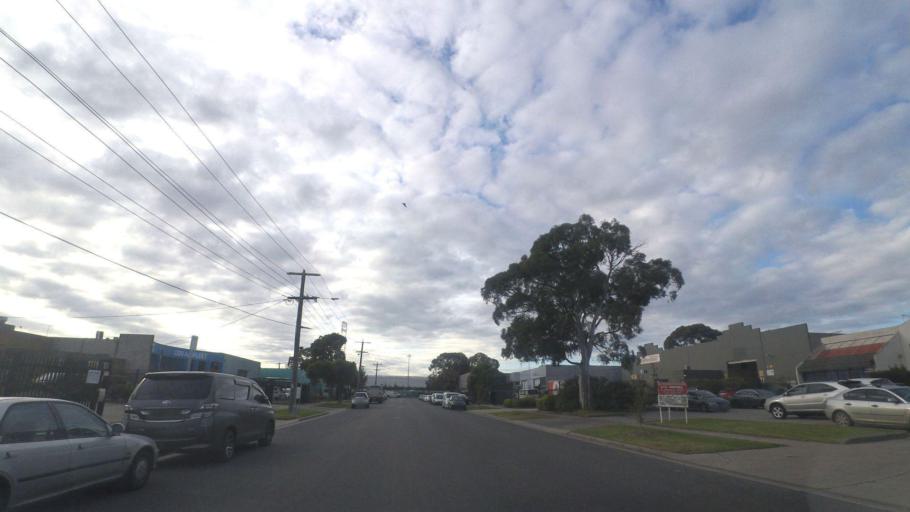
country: AU
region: Victoria
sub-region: Kingston
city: Clayton South
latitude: -37.9423
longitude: 145.1219
